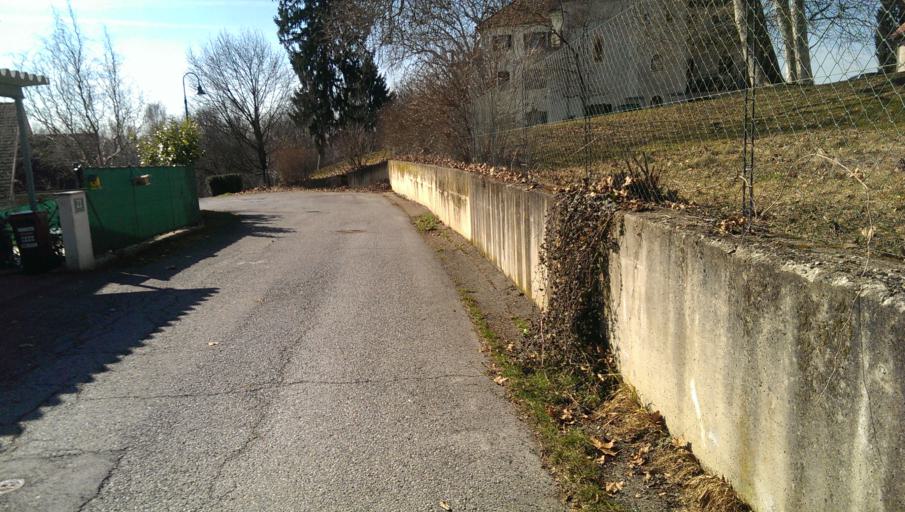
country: AT
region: Styria
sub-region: Graz Stadt
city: Graz
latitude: 47.0631
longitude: 15.4767
